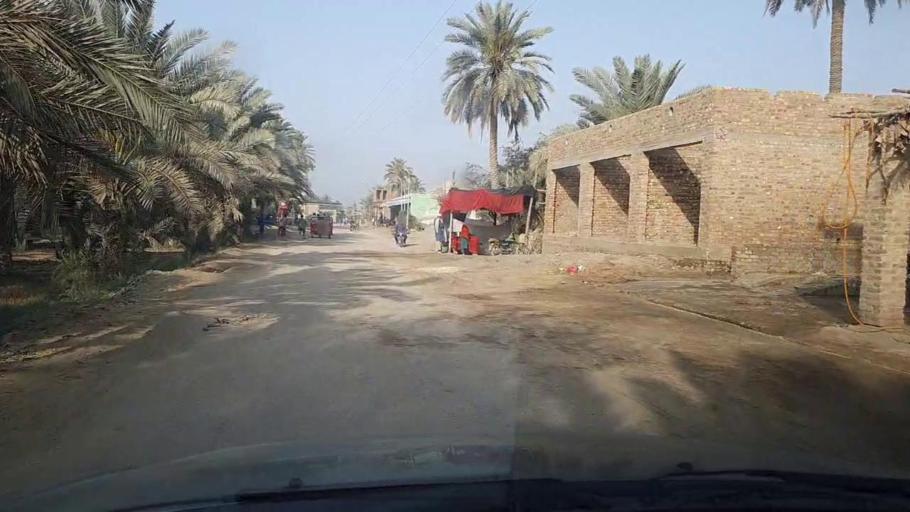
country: PK
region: Sindh
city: Pir jo Goth
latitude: 27.5583
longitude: 68.5620
